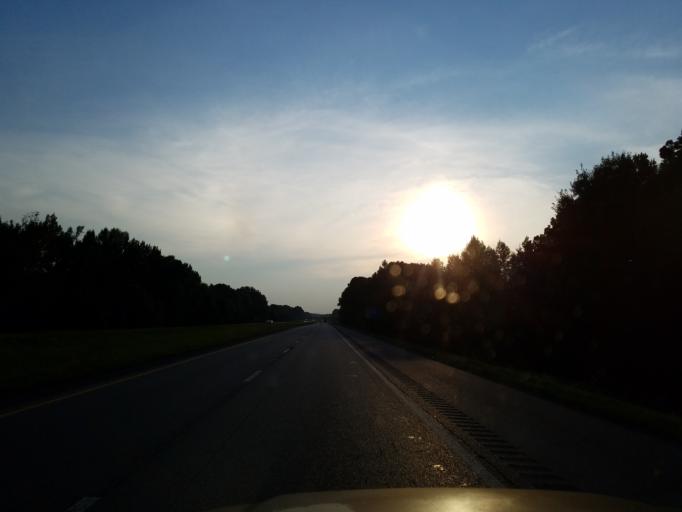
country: US
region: Mississippi
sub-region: Lauderdale County
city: Marion
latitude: 32.4137
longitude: -88.4967
